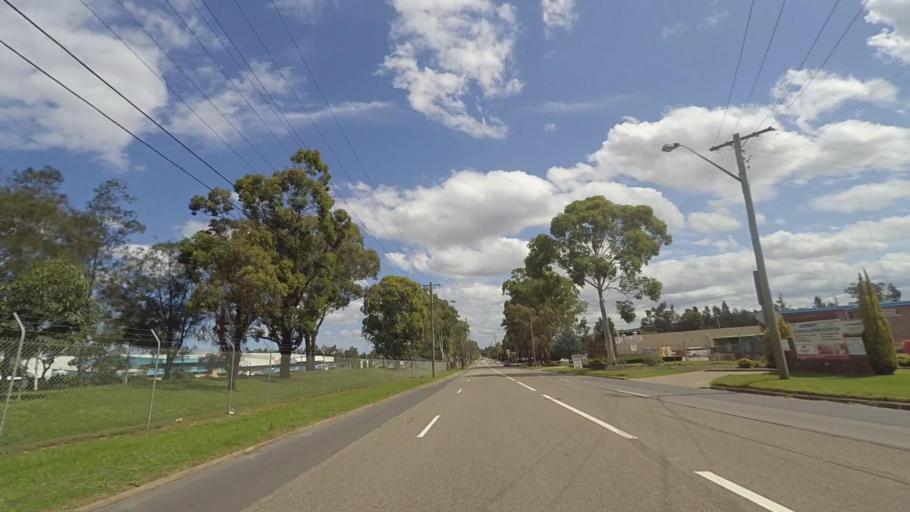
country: AU
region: New South Wales
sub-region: Holroyd
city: Guildford West
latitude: -33.8541
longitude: 150.9597
